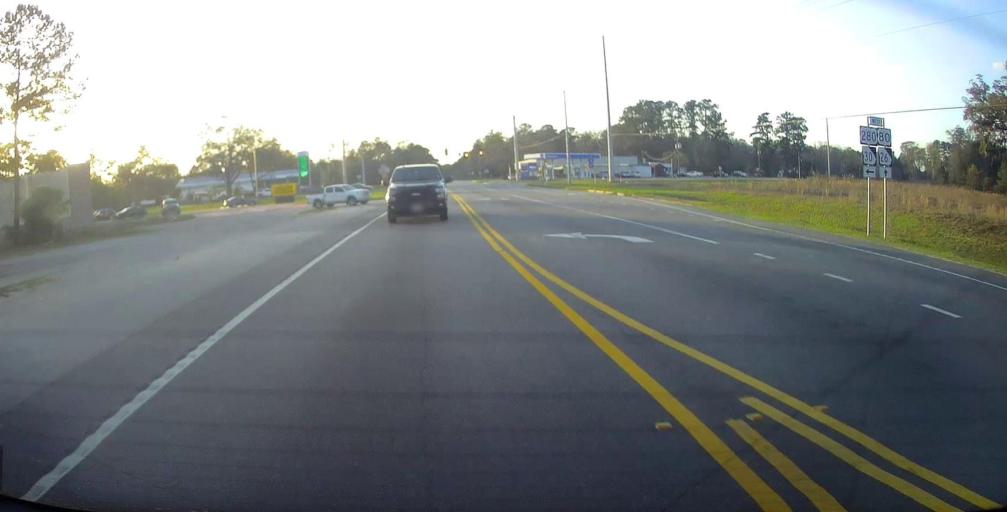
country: US
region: Georgia
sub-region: Effingham County
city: Guyton
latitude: 32.1966
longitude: -81.4371
